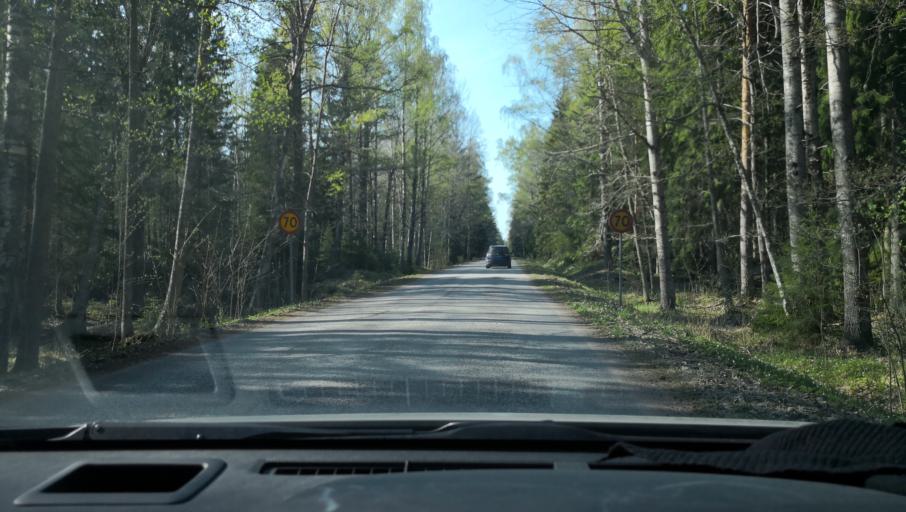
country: SE
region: Uppsala
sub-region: Heby Kommun
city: Tarnsjo
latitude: 60.2708
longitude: 16.9069
